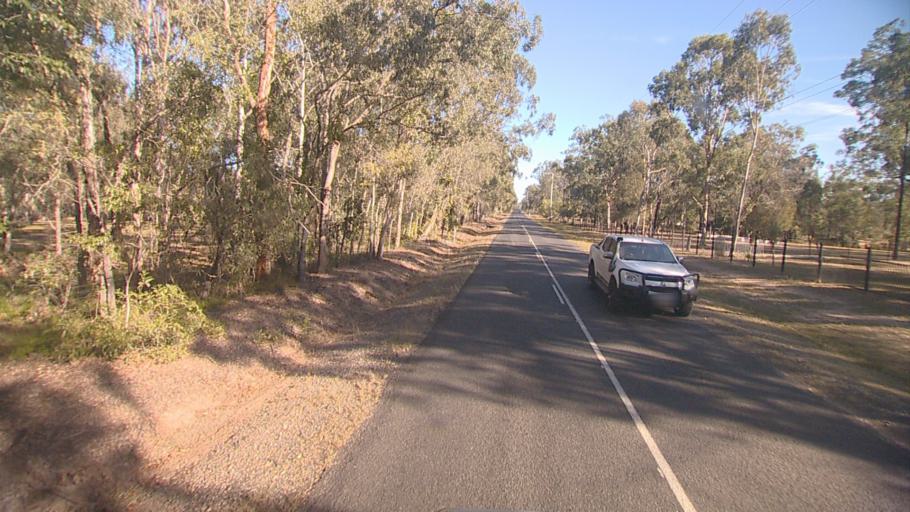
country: AU
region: Queensland
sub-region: Ipswich
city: Springfield Lakes
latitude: -27.6950
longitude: 152.9425
